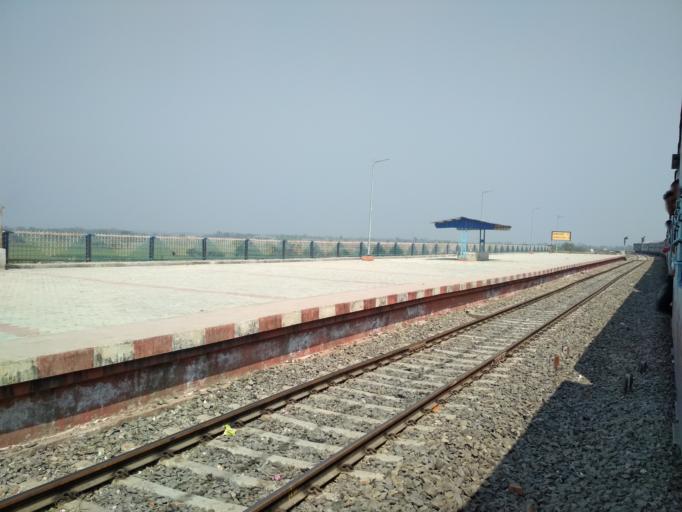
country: IN
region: Bihar
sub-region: Munger
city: Munger
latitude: 25.4275
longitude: 86.4378
